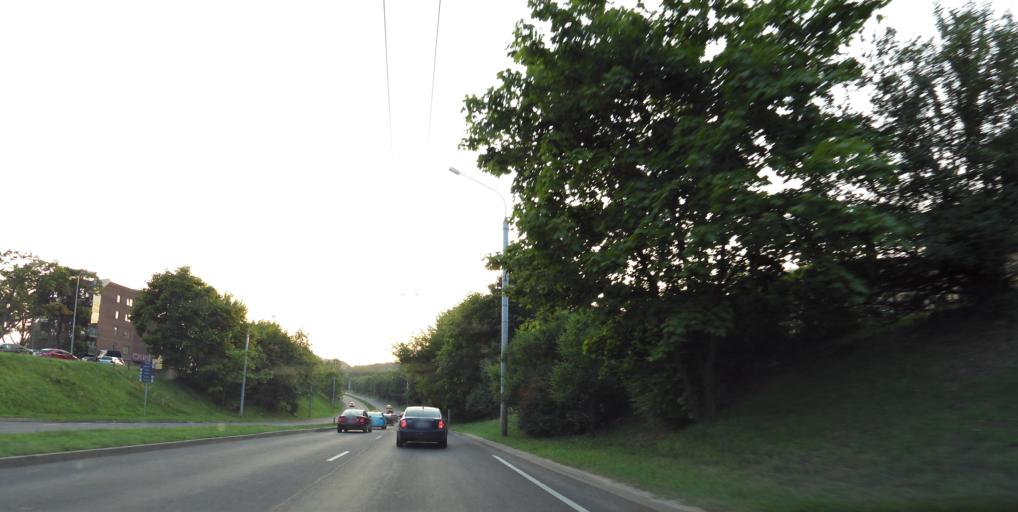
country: LT
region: Vilnius County
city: Seskine
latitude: 54.6996
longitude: 25.2525
